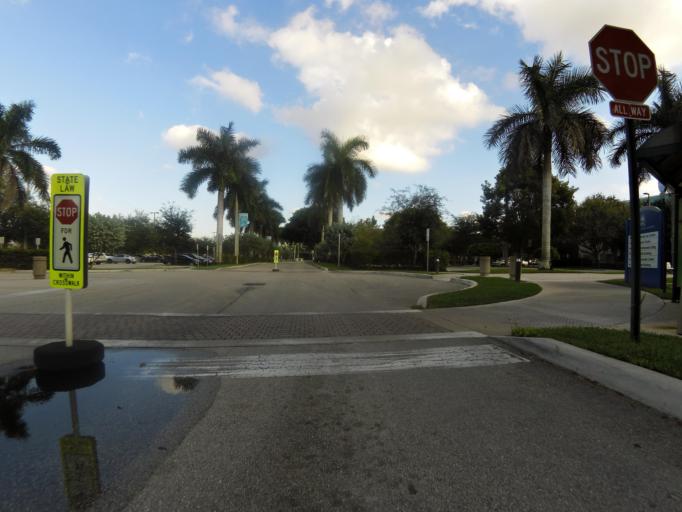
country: US
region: Florida
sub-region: Broward County
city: Davie
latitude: 26.0807
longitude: -80.2409
